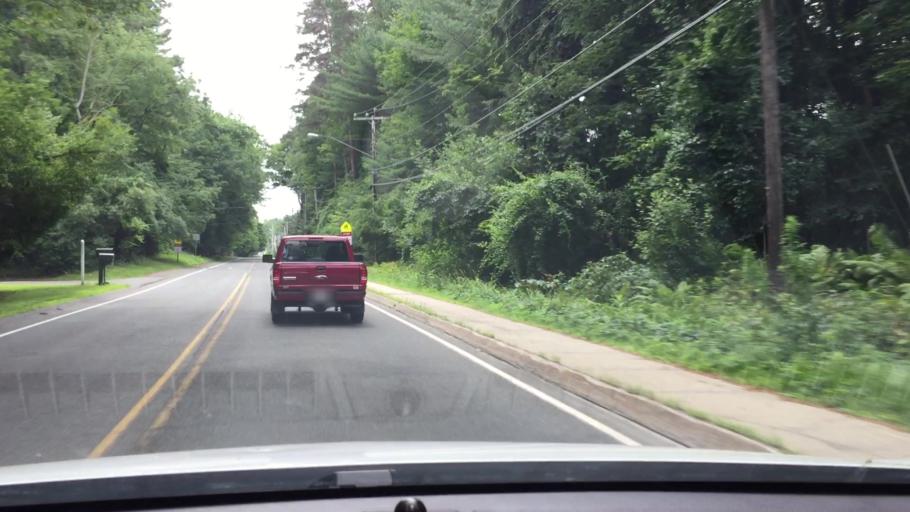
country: US
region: Massachusetts
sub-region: Berkshire County
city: Pittsfield
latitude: 42.4238
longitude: -73.2441
